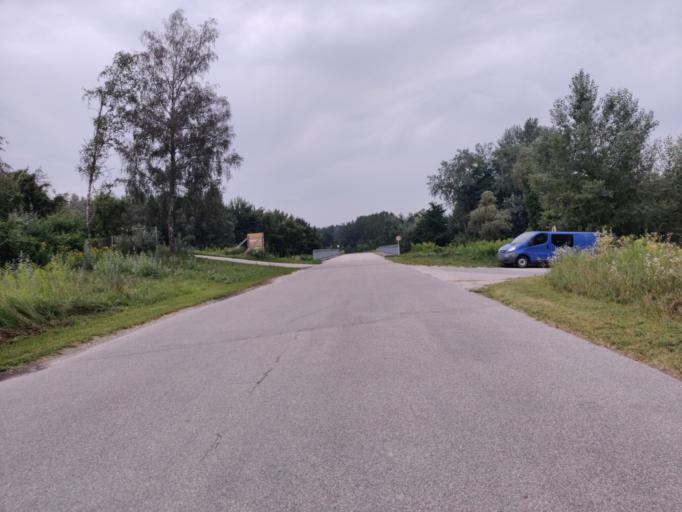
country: AT
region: Upper Austria
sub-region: Politischer Bezirk Linz-Land
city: Asten
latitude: 48.2431
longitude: 14.4261
